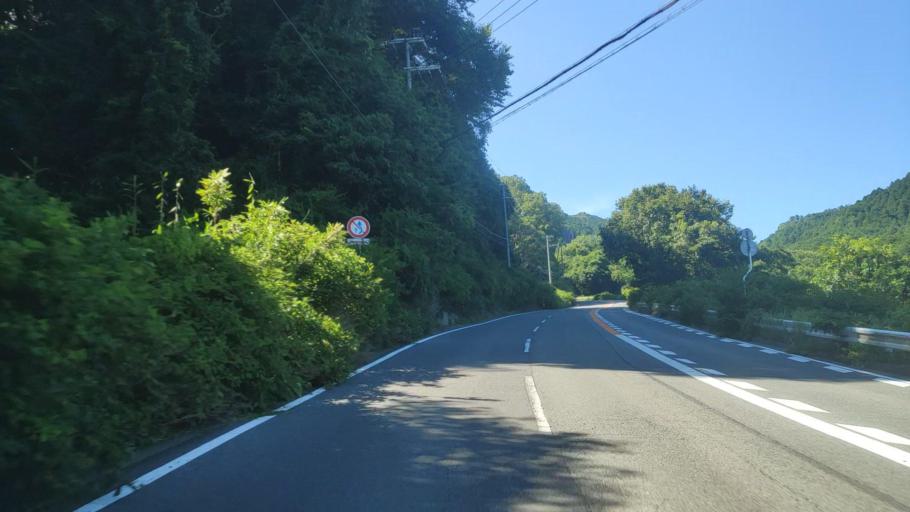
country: JP
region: Nara
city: Haibara-akanedai
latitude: 34.5508
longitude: 135.9588
